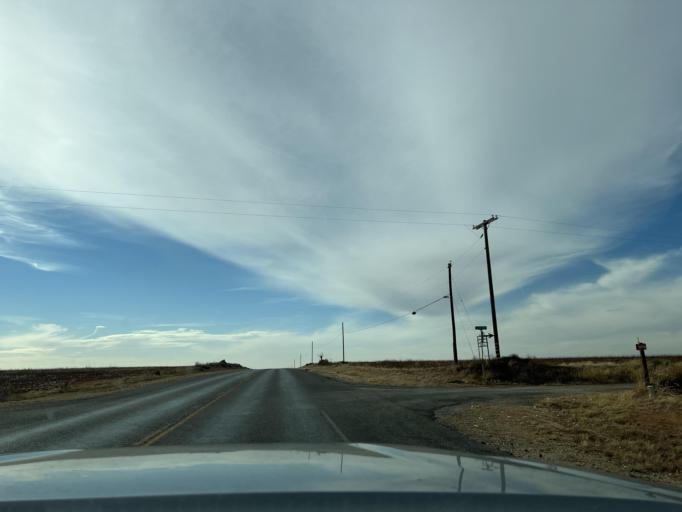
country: US
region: Texas
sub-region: Fisher County
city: Roby
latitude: 32.7416
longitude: -100.4560
